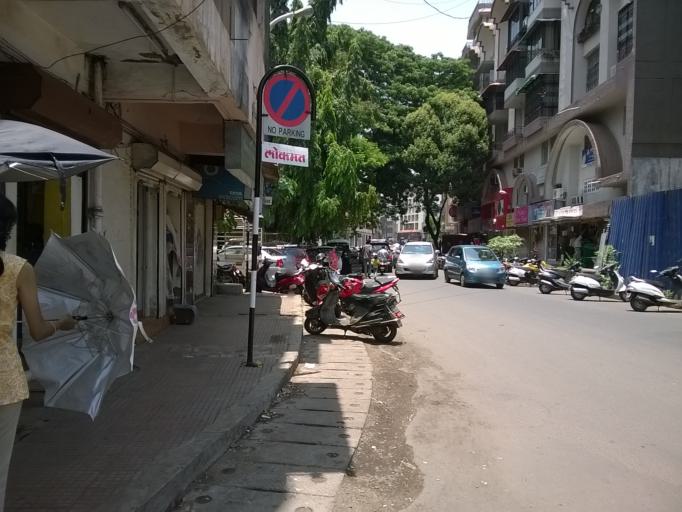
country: IN
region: Goa
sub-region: North Goa
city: Panaji
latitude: 15.4972
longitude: 73.8226
